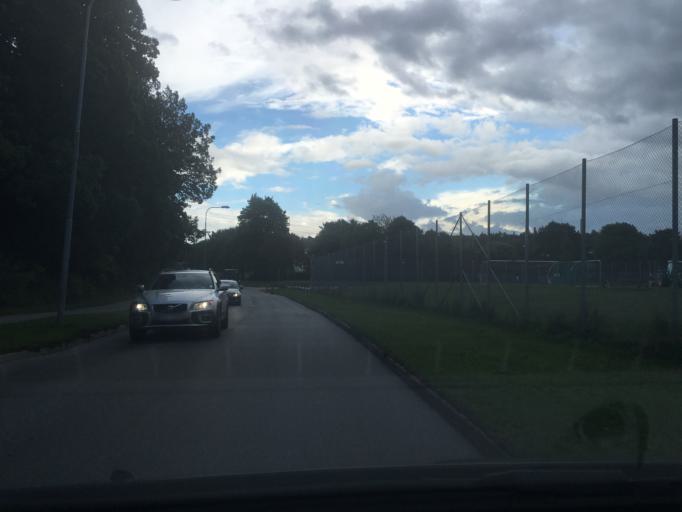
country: SE
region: Stockholm
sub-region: Stockholms Kommun
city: Bromma
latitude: 59.3377
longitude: 17.9271
